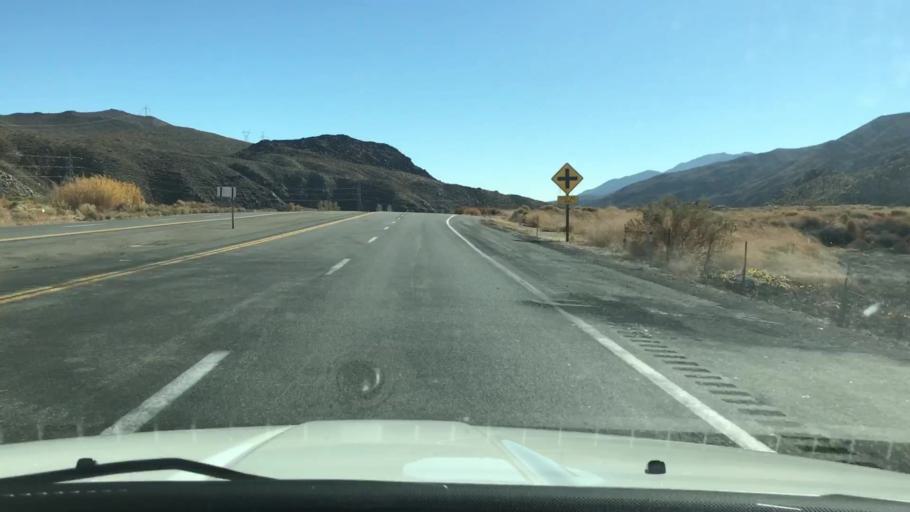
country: US
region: California
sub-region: Kern County
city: Inyokern
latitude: 35.9407
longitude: -117.9067
